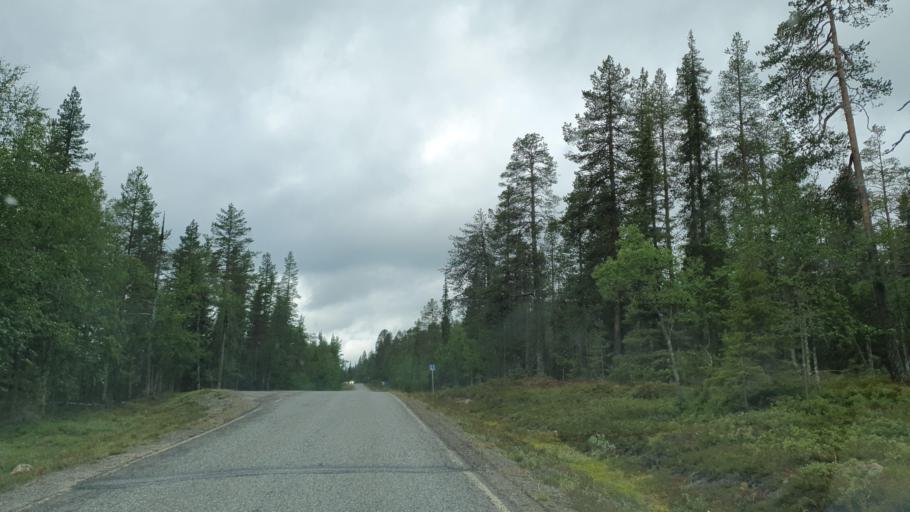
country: FI
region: Lapland
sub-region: Tunturi-Lappi
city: Muonio
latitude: 67.7286
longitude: 24.2484
